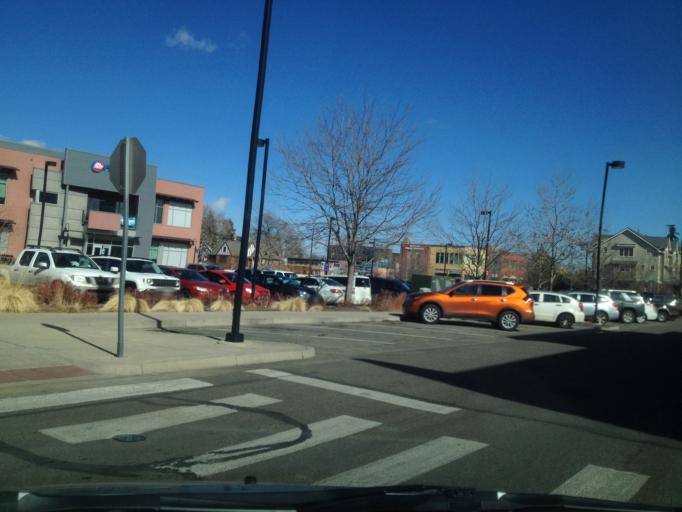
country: US
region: Colorado
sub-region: Jefferson County
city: Edgewater
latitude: 39.7686
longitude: -105.0474
